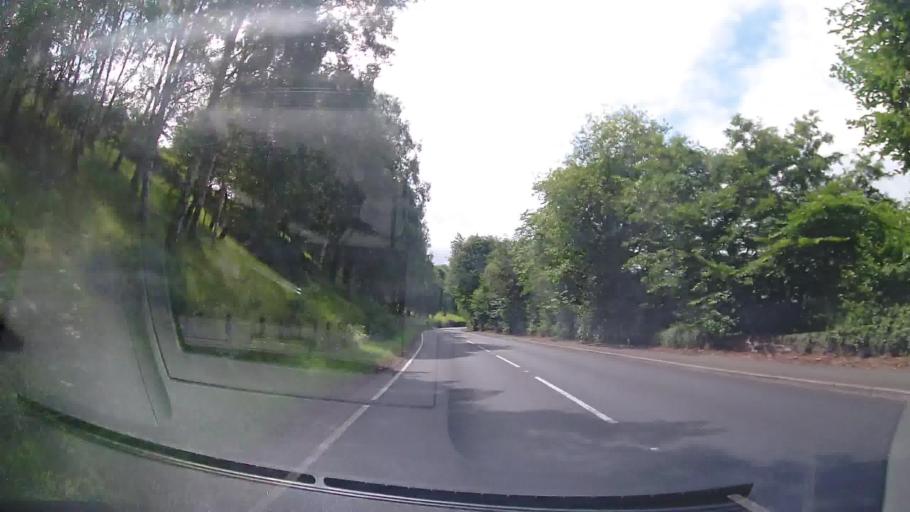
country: GB
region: Wales
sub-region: Denbighshire
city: Corwen
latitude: 52.9775
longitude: -3.3242
